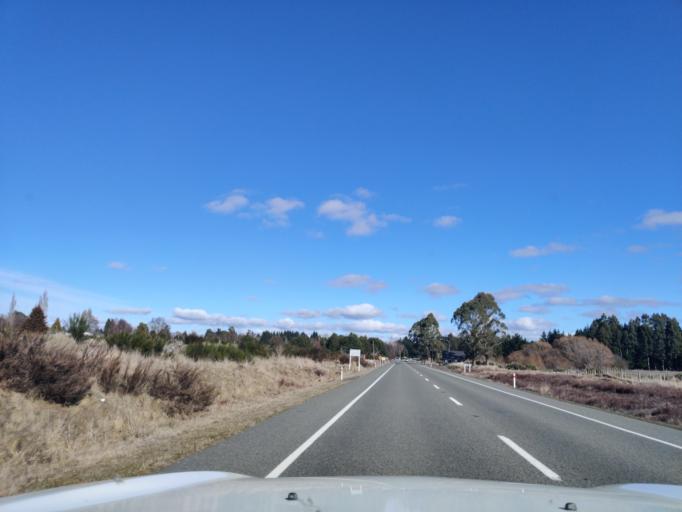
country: NZ
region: Manawatu-Wanganui
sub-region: Ruapehu District
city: Waiouru
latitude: -39.4625
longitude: 175.6741
